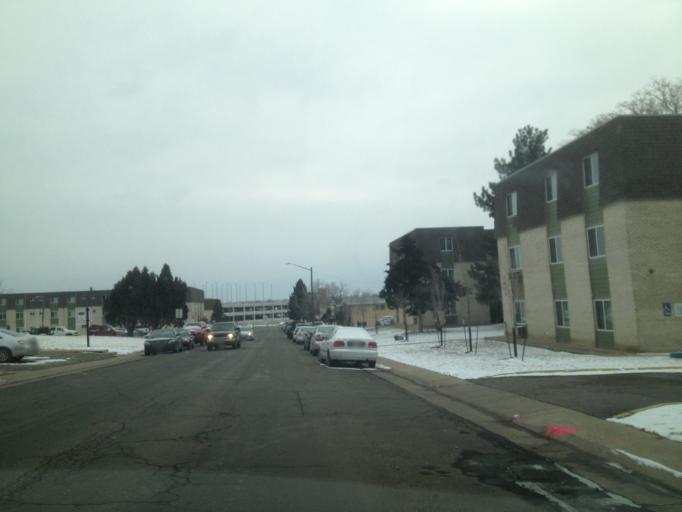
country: US
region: Colorado
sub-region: Adams County
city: Westminster
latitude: 39.8263
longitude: -105.0280
